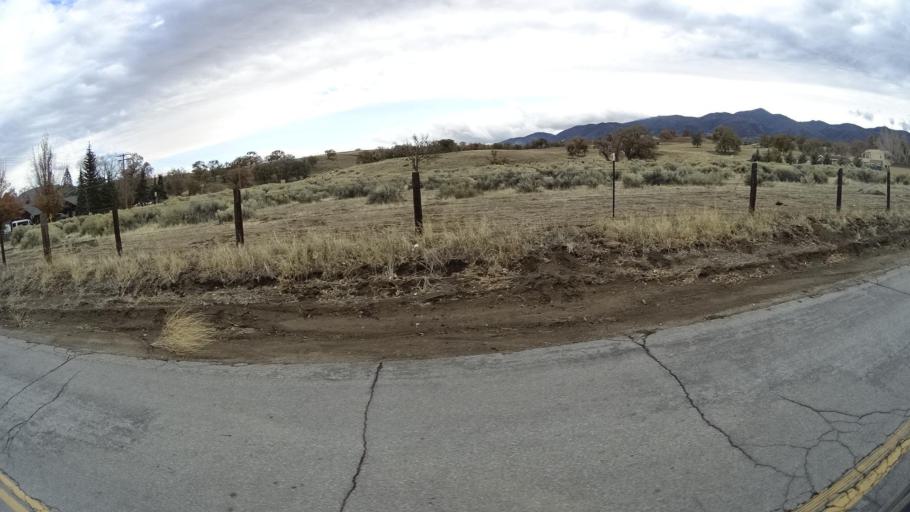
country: US
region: California
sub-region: Kern County
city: Golden Hills
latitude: 35.1367
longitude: -118.5047
